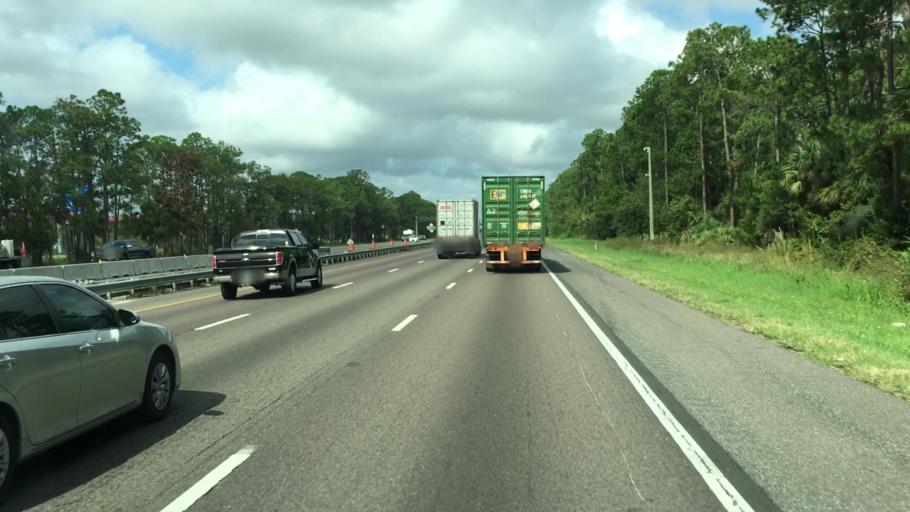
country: US
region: Florida
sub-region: Volusia County
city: Daytona Beach
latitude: 29.1906
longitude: -81.0928
